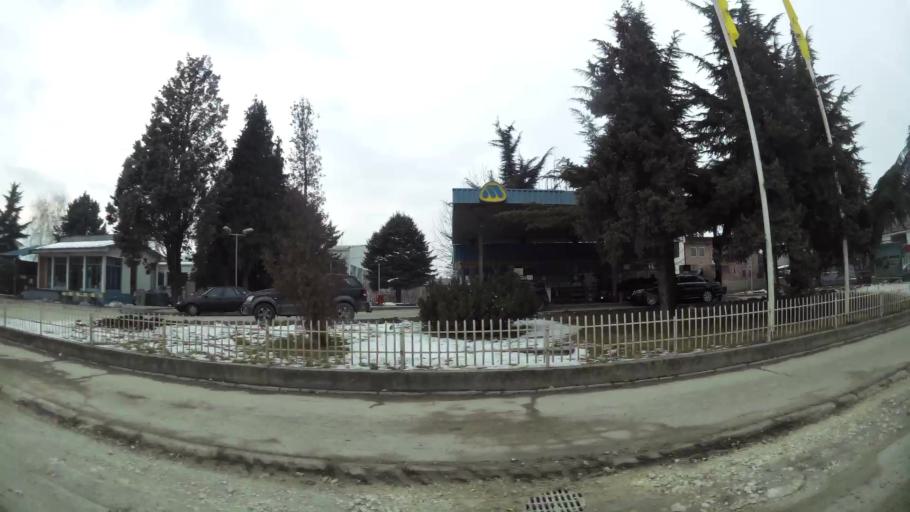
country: MK
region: Butel
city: Butel
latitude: 42.0297
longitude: 21.4447
